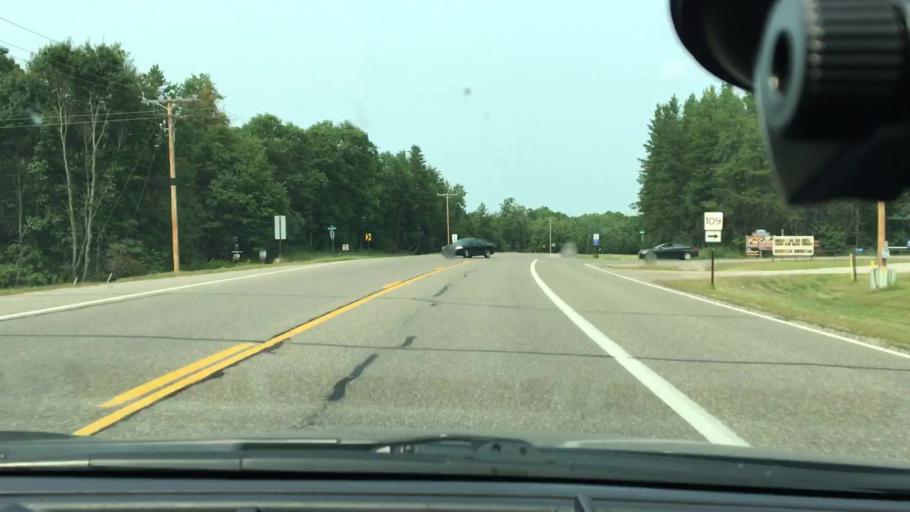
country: US
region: Minnesota
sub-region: Crow Wing County
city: Breezy Point
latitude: 46.5585
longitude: -94.1356
